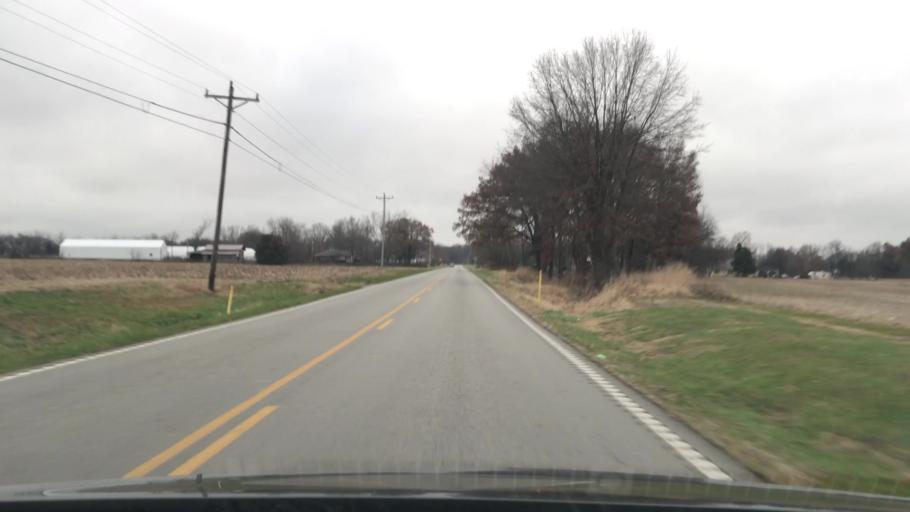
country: US
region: Kentucky
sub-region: Todd County
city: Guthrie
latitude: 36.7171
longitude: -87.1917
